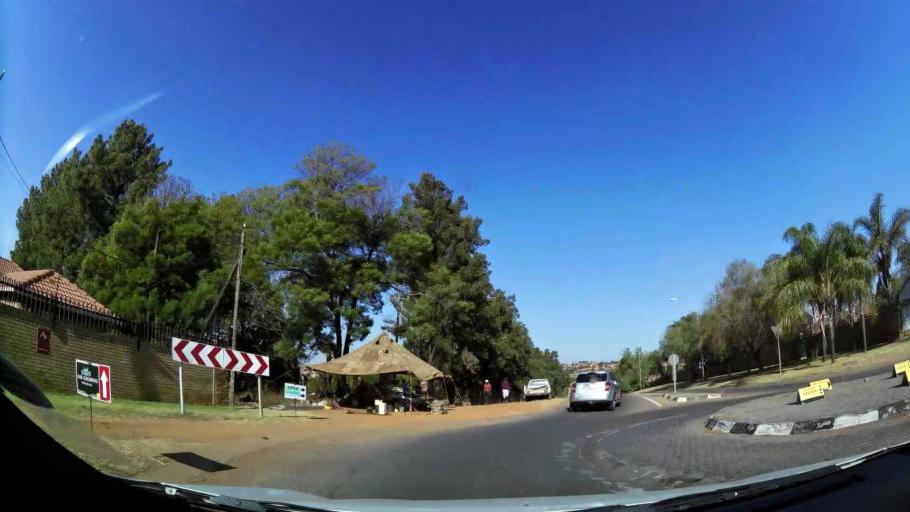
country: ZA
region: Gauteng
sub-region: City of Tshwane Metropolitan Municipality
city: Centurion
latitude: -25.8342
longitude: 28.2998
